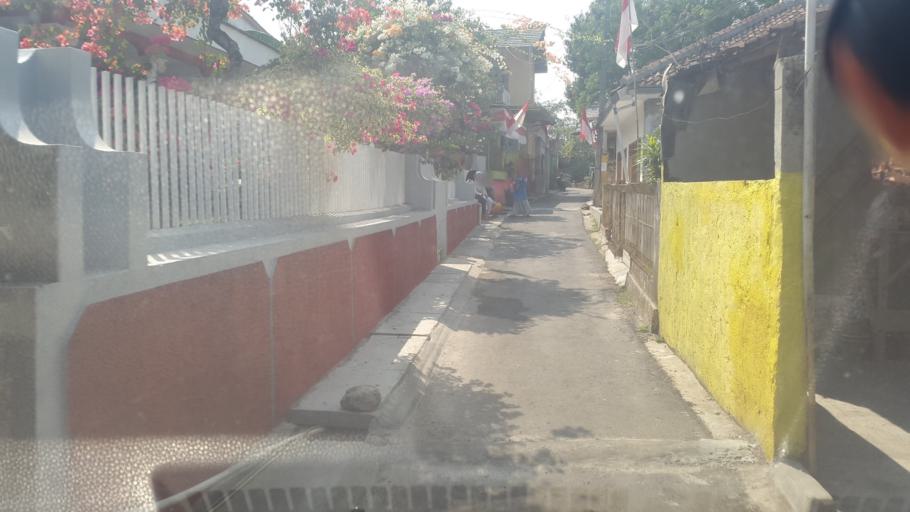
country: ID
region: West Java
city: Gunungkalong
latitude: -6.8914
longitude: 106.7848
